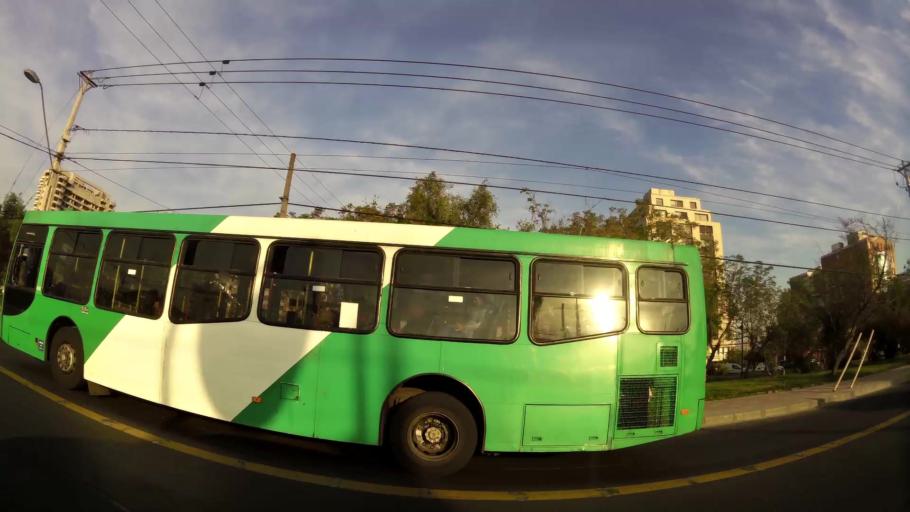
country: CL
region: Santiago Metropolitan
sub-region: Provincia de Santiago
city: Santiago
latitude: -33.4912
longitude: -70.6516
